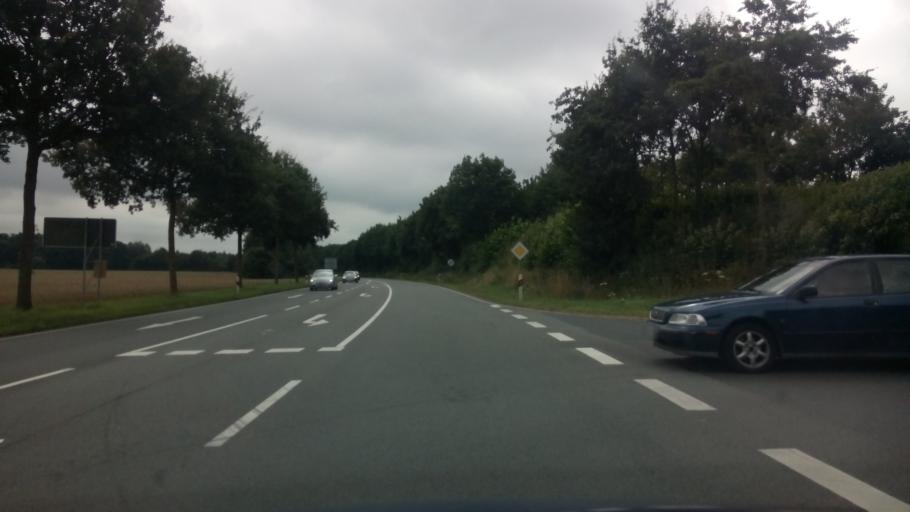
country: DE
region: Lower Saxony
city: Bassum
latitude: 52.8711
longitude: 8.7282
